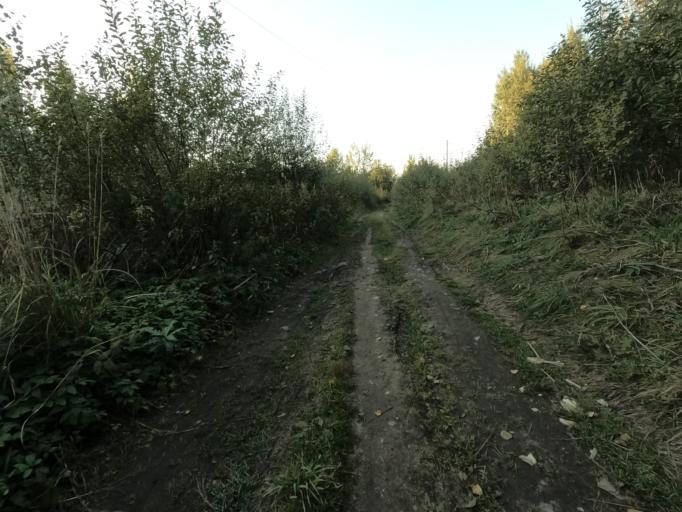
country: RU
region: Leningrad
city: Nikol'skoye
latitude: 59.7142
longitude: 30.7972
